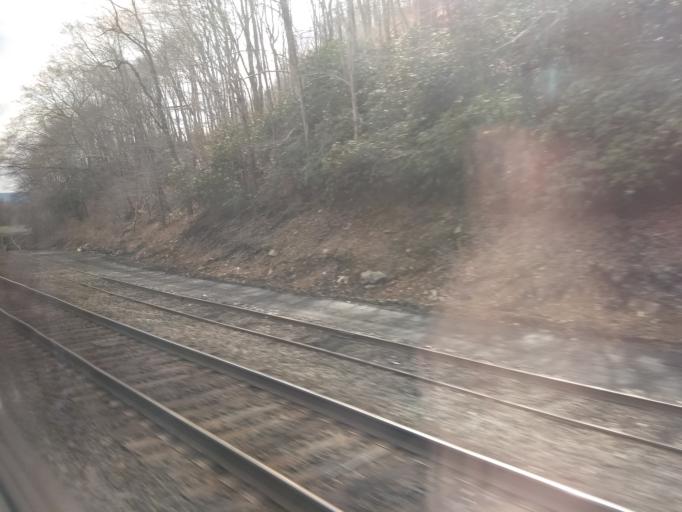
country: US
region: Pennsylvania
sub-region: Huntingdon County
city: Mount Union
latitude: 40.3905
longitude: -77.8951
